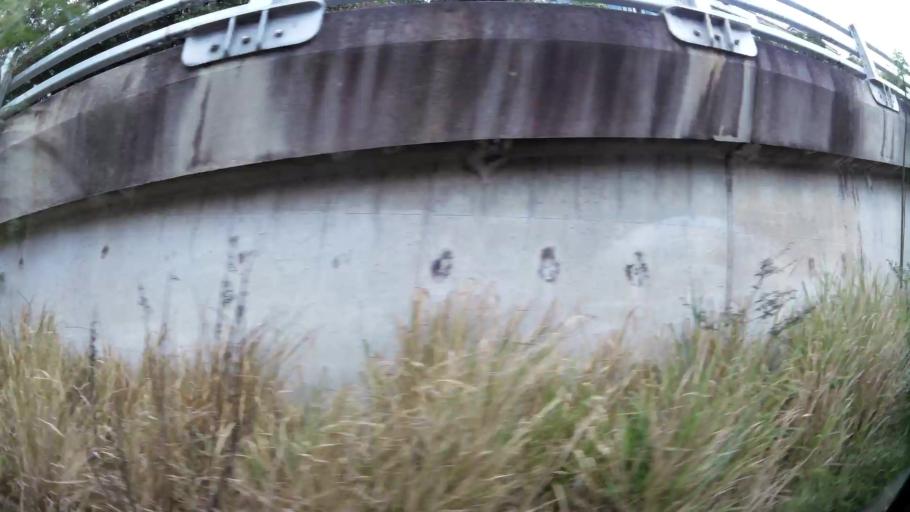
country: HK
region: Sham Shui Po
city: Sham Shui Po
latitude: 22.3429
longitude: 114.1559
